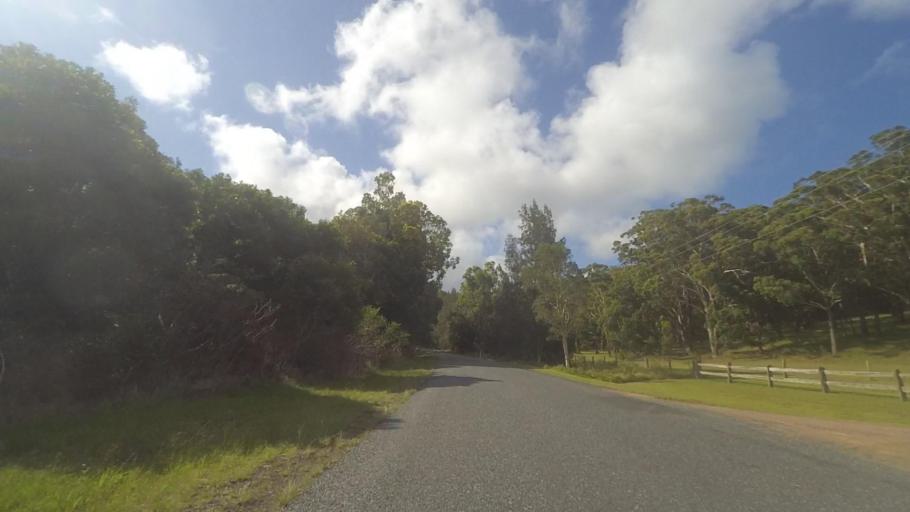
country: AU
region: New South Wales
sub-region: Great Lakes
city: Forster
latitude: -32.3983
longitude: 152.4592
